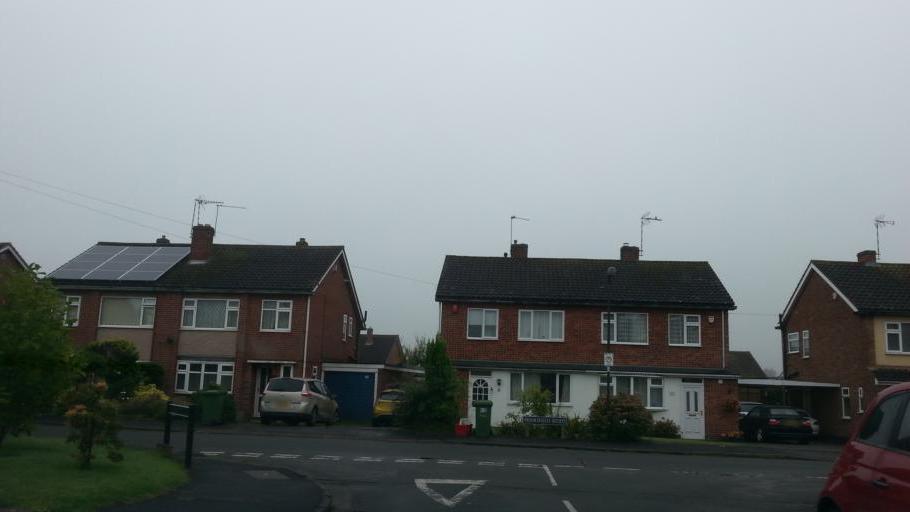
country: GB
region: England
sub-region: Warwickshire
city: Kenilworth
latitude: 52.3546
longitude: -1.5901
